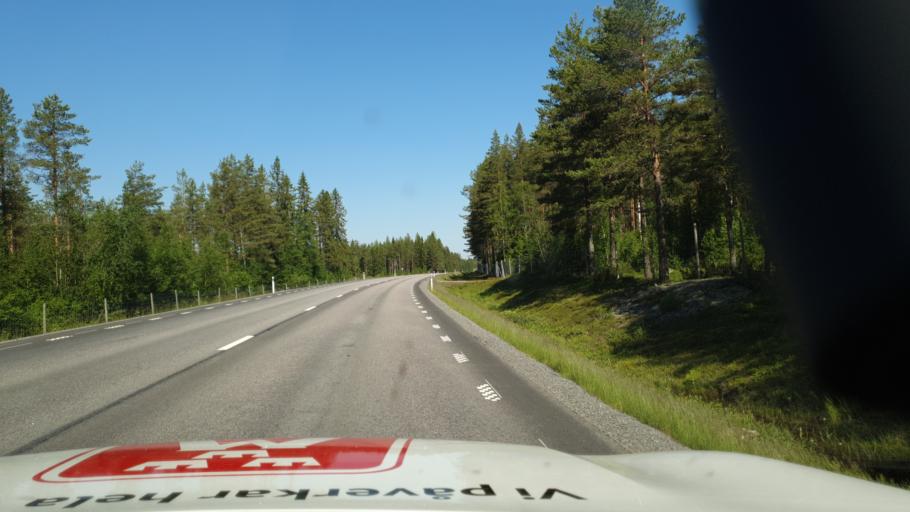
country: SE
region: Vaesterbotten
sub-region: Skelleftea Kommun
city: Burea
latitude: 64.4898
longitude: 21.2729
